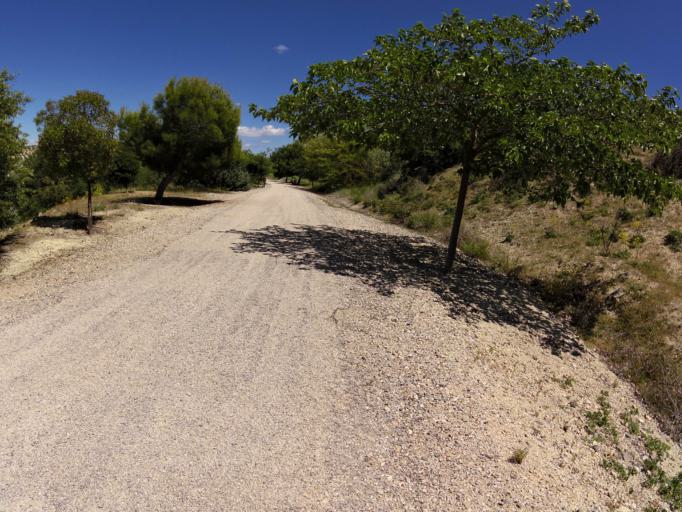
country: ES
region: Andalusia
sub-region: Provincia de Jaen
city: Jamilena
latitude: 37.7714
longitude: -3.9293
